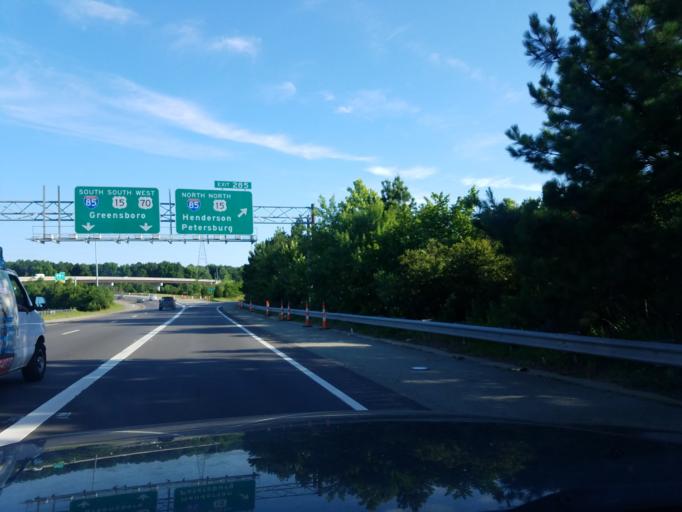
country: US
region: North Carolina
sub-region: Durham County
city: Durham
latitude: 36.0110
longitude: -78.8677
